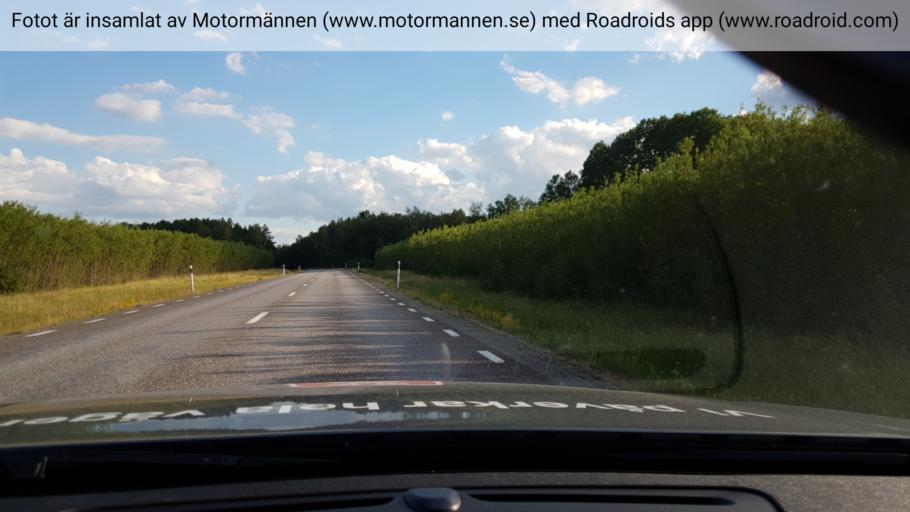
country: SE
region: Uppsala
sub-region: Heby Kommun
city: Morgongava
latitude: 59.8486
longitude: 16.9273
